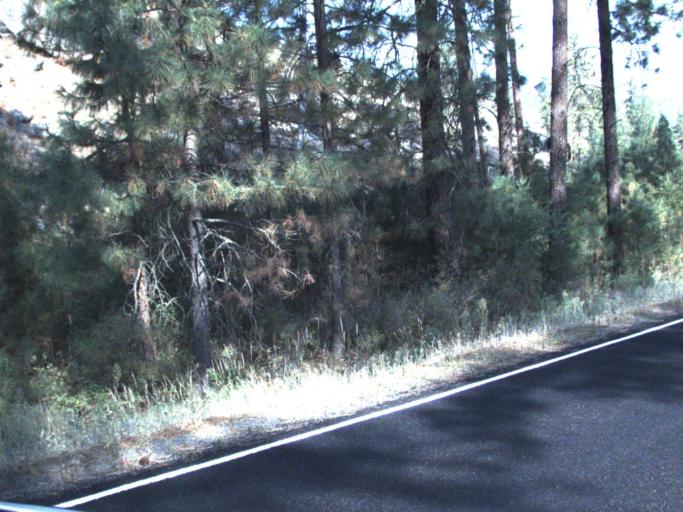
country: US
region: Washington
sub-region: Spokane County
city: Airway Heights
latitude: 47.8605
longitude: -117.7121
